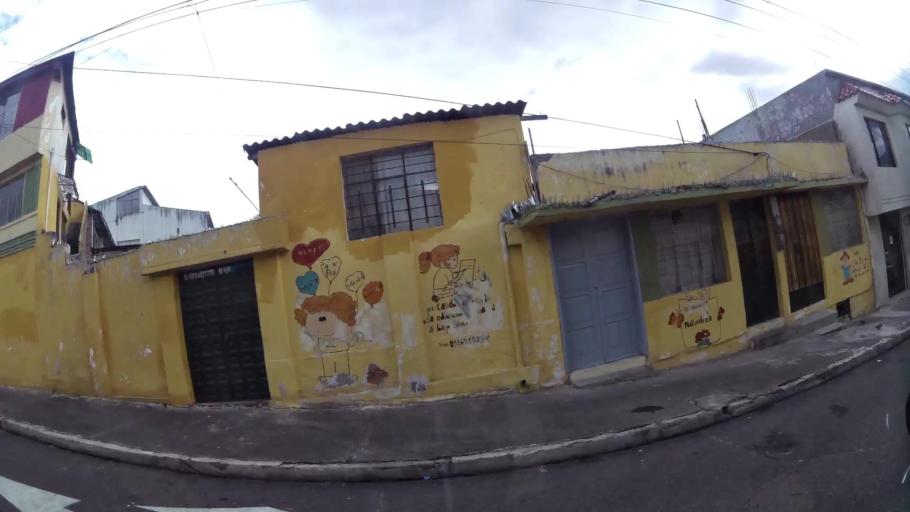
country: EC
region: Pichincha
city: Quito
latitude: -0.2465
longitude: -78.5115
